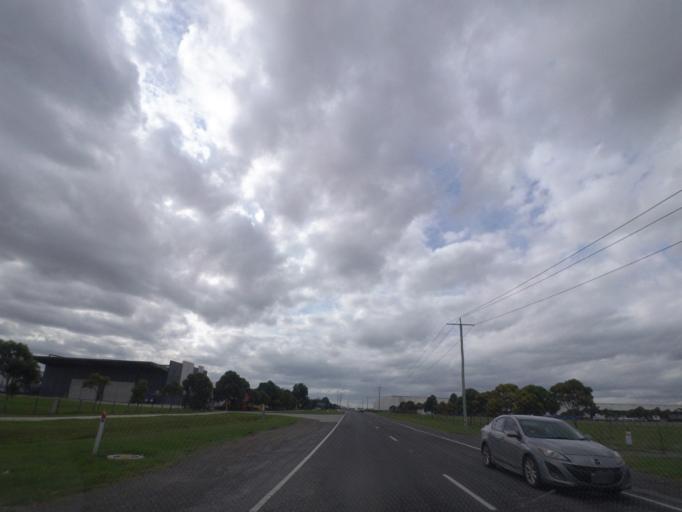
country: AU
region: Victoria
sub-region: Brimbank
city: Keilor Park
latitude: -37.7025
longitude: 144.8578
